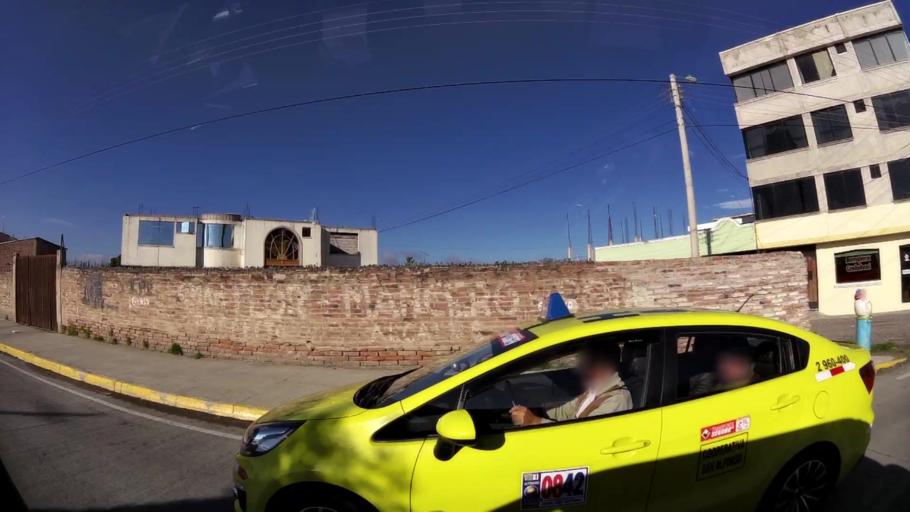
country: EC
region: Chimborazo
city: Riobamba
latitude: -1.6766
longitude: -78.6301
